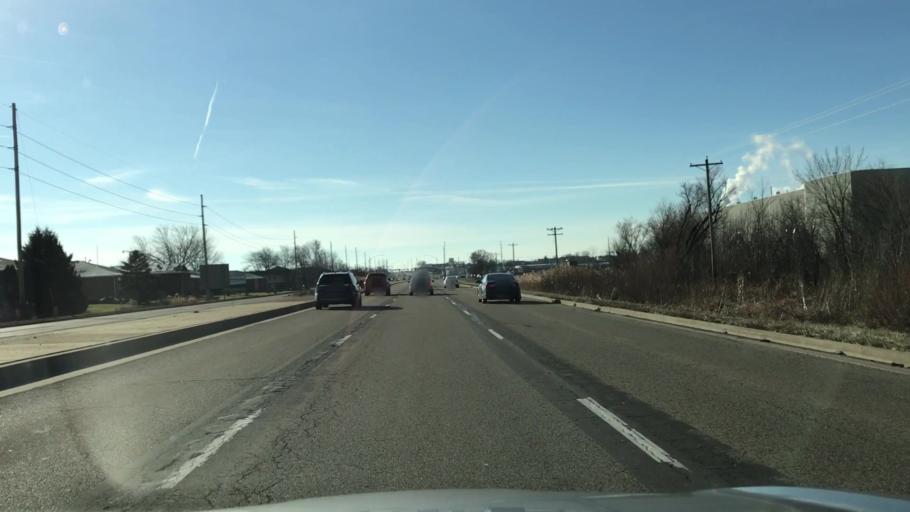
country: US
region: Illinois
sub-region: McLean County
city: Normal
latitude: 40.5225
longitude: -88.9526
